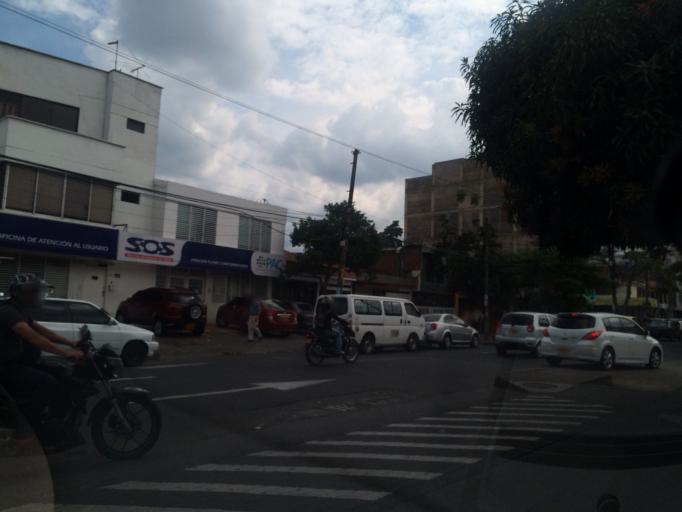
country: CO
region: Valle del Cauca
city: Cali
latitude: 3.4246
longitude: -76.5468
